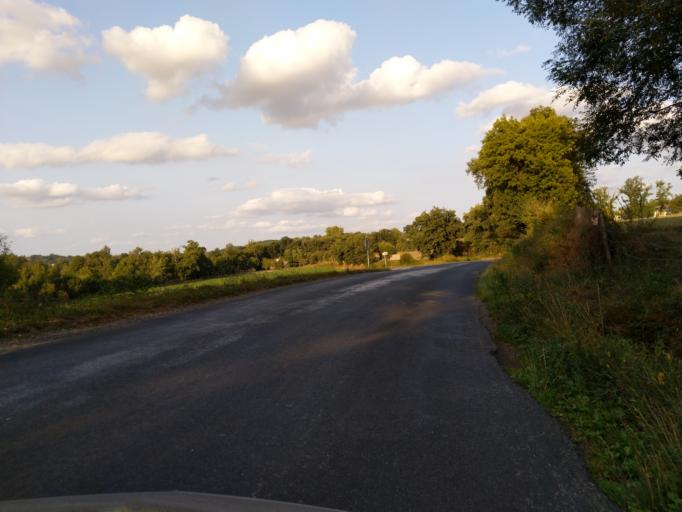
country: FR
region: Midi-Pyrenees
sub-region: Departement du Tarn
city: Frejairolles
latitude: 43.8347
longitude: 2.2080
